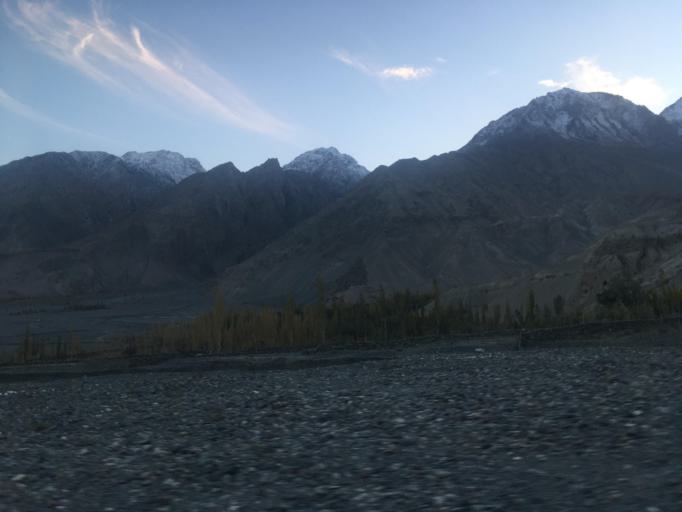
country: PK
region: Gilgit-Baltistan
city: Skardu
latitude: 35.3067
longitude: 75.5353
